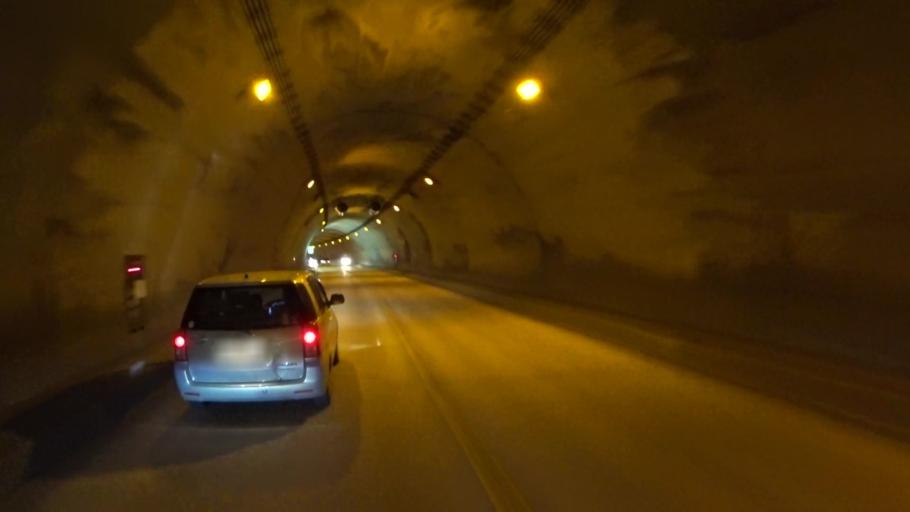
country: JP
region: Kyoto
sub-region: Kyoto-shi
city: Kamigyo-ku
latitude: 35.0899
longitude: 135.6871
